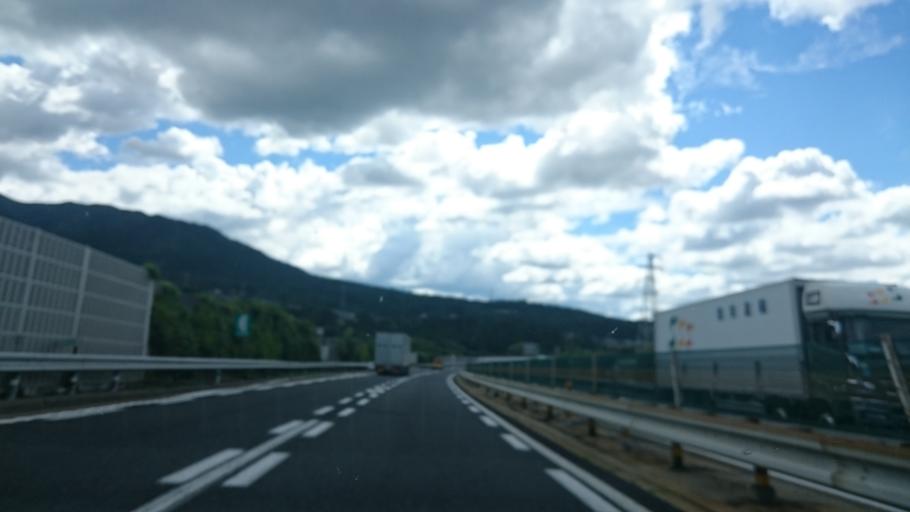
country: JP
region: Gifu
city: Nakatsugawa
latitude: 35.4799
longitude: 137.5077
